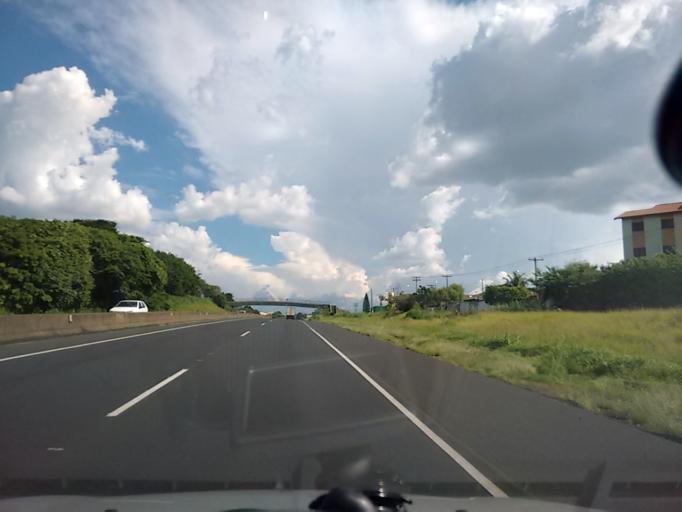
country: BR
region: Sao Paulo
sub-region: Marilia
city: Marilia
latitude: -22.1931
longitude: -49.9663
